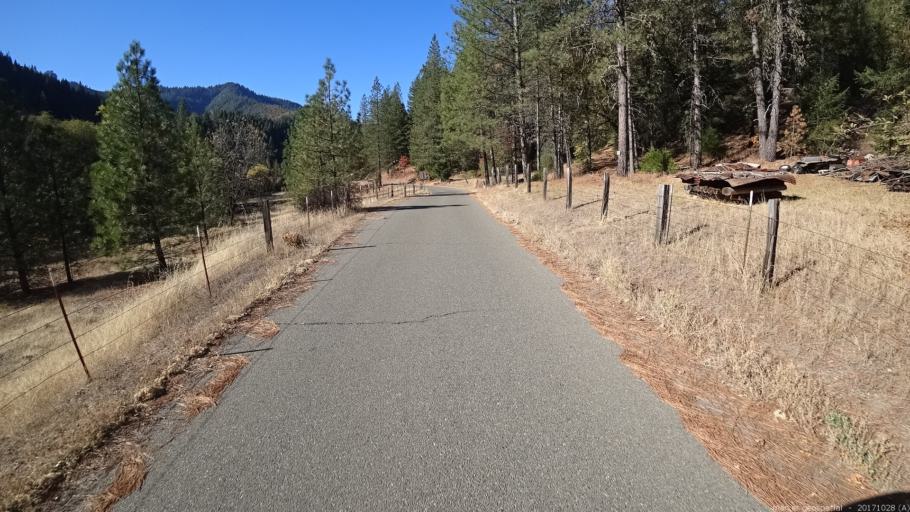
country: US
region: California
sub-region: Shasta County
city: Shasta
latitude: 40.7603
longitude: -122.5715
